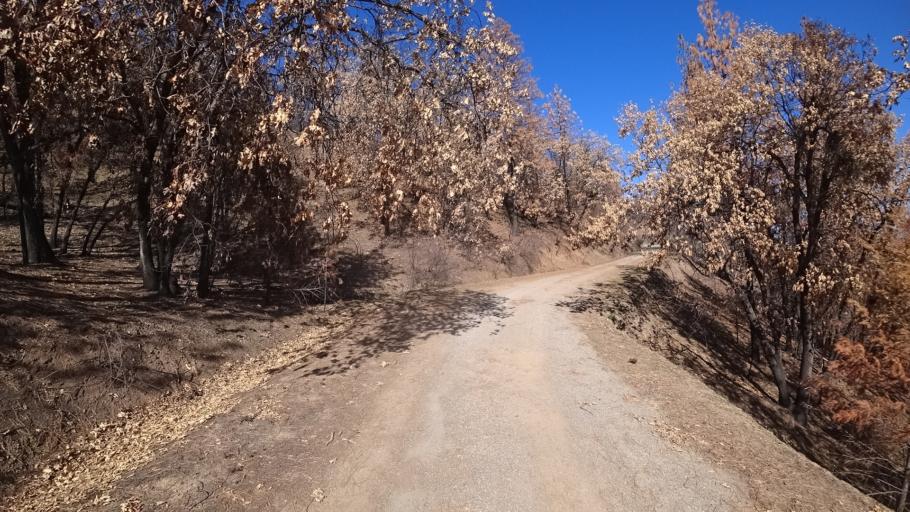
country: US
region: California
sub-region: Tehama County
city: Rancho Tehama Reserve
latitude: 39.6705
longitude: -122.6930
